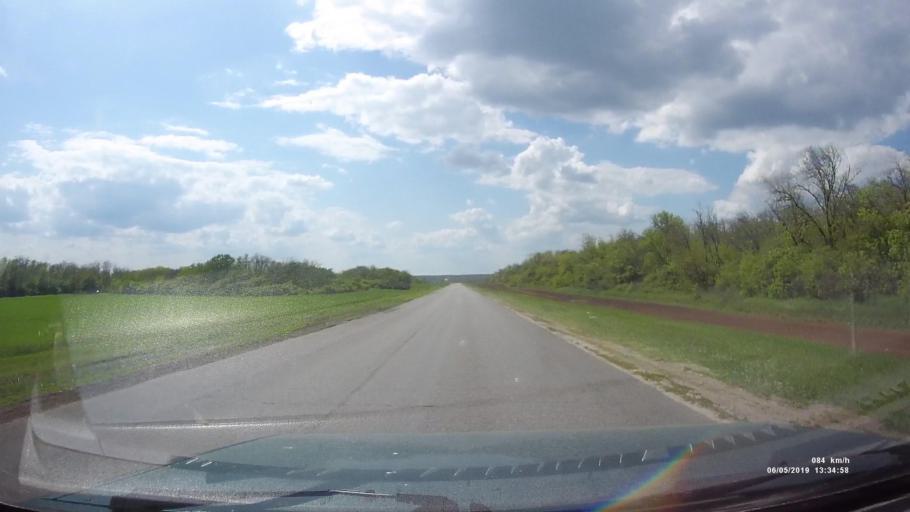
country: RU
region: Rostov
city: Ust'-Donetskiy
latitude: 47.6936
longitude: 40.7542
